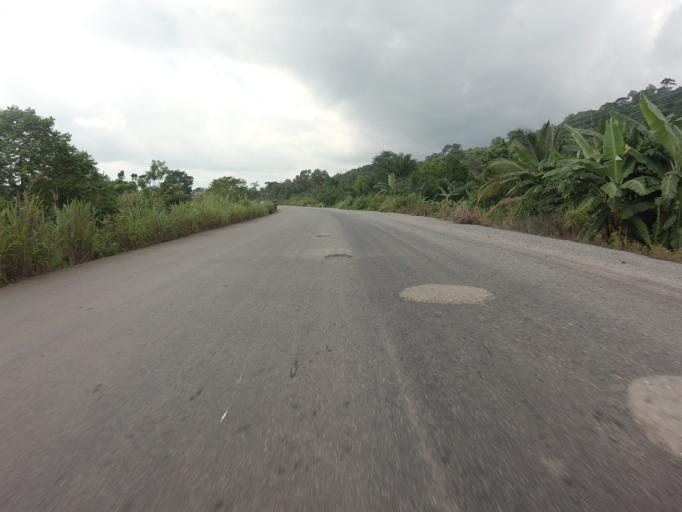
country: GH
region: Volta
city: Kpandu
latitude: 6.9063
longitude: 0.4438
